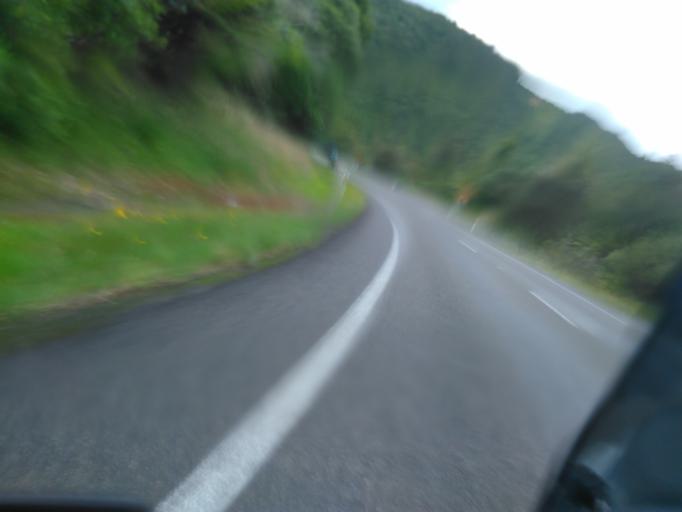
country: NZ
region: Bay of Plenty
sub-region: Opotiki District
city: Opotiki
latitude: -38.2399
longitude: 177.3083
